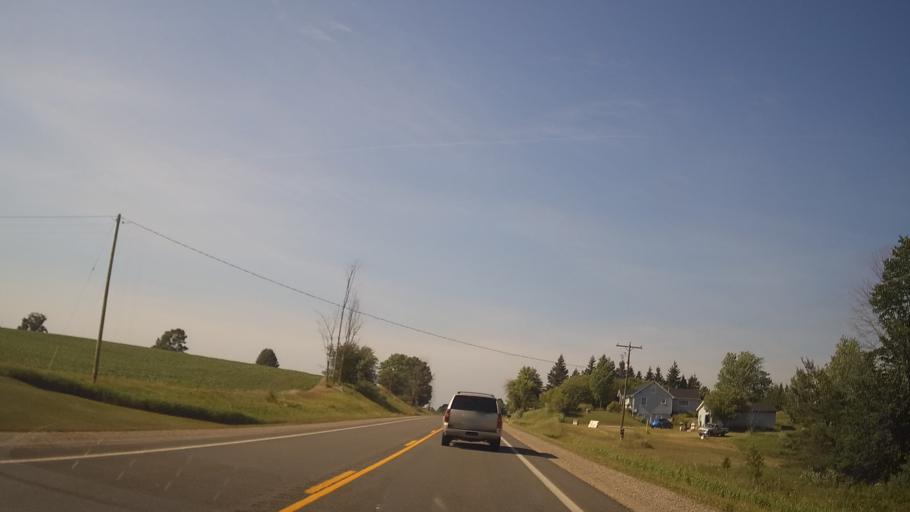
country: US
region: Michigan
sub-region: Ogemaw County
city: West Branch
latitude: 44.3753
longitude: -84.1159
